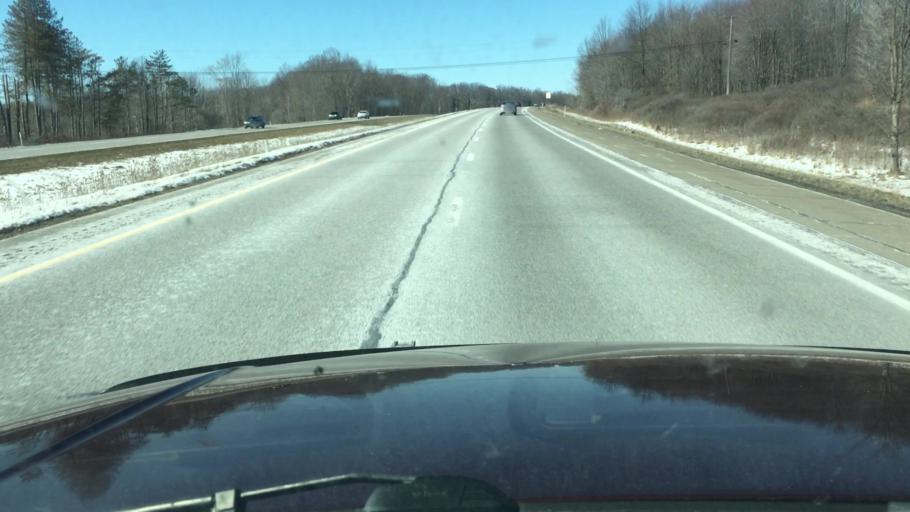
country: US
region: Pennsylvania
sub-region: Crawford County
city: Cochranton
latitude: 41.4613
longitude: -80.1653
